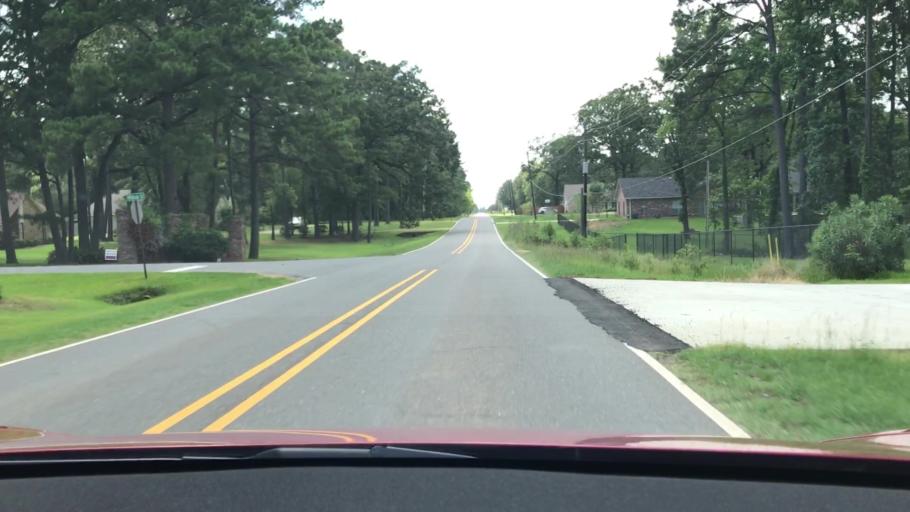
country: US
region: Louisiana
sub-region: De Soto Parish
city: Stonewall
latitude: 32.3693
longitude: -93.7077
